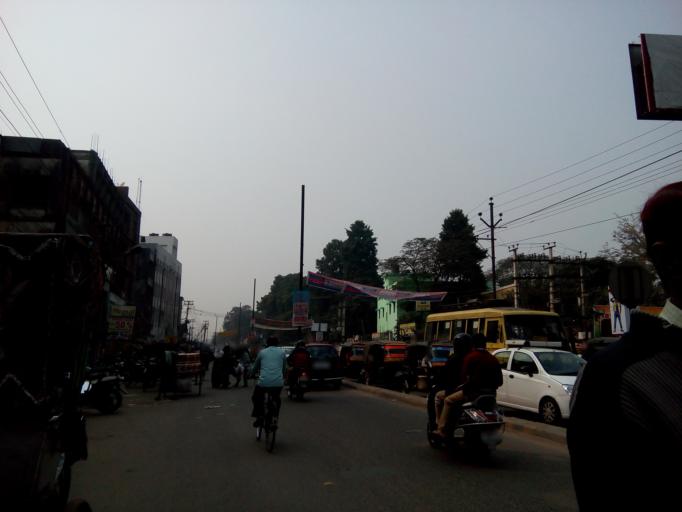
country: IN
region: Bihar
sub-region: Patna
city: Patna
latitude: 25.6191
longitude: 85.1524
